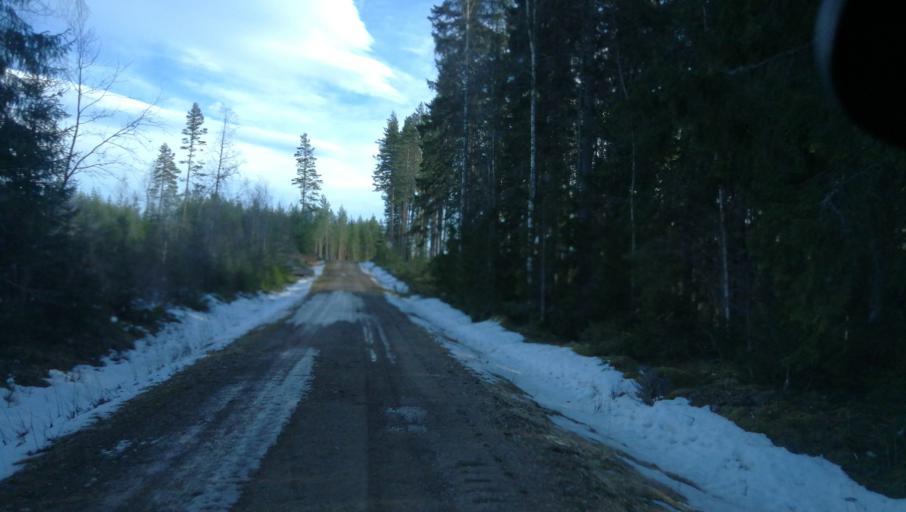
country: SE
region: Dalarna
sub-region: Vansbro Kommun
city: Vansbro
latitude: 60.8104
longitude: 14.2059
